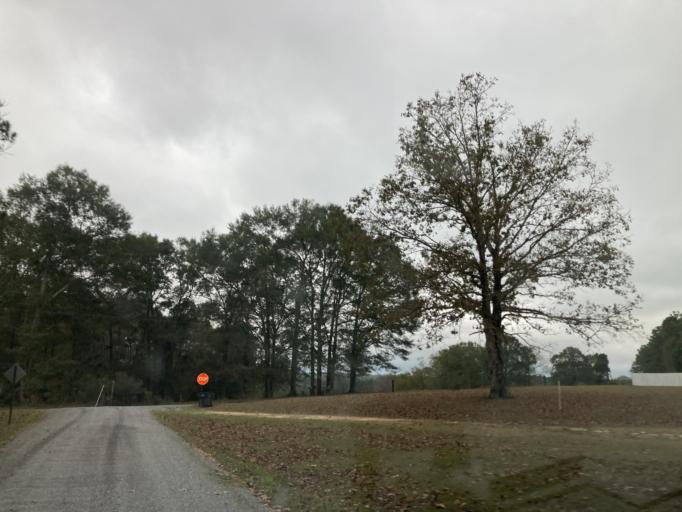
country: US
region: Mississippi
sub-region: Lamar County
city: Purvis
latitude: 31.1862
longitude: -89.4464
